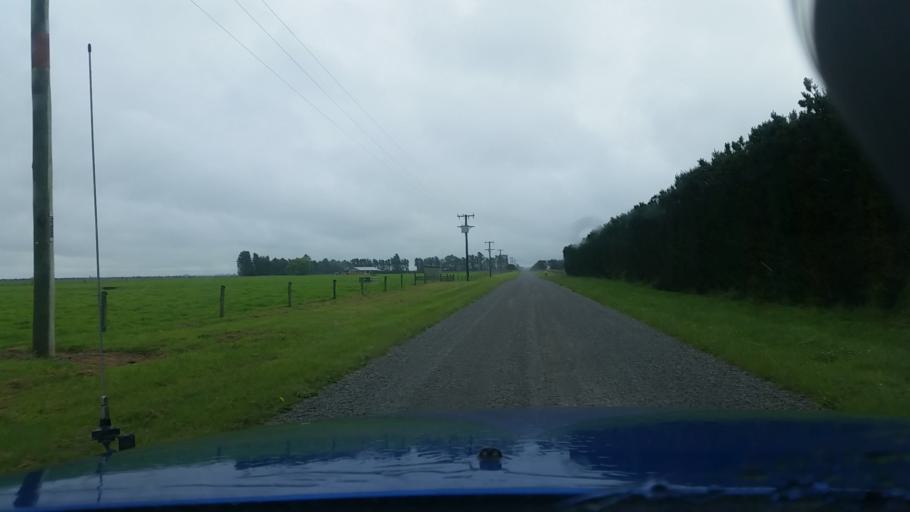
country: NZ
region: Canterbury
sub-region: Ashburton District
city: Tinwald
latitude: -43.8970
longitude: 171.5749
